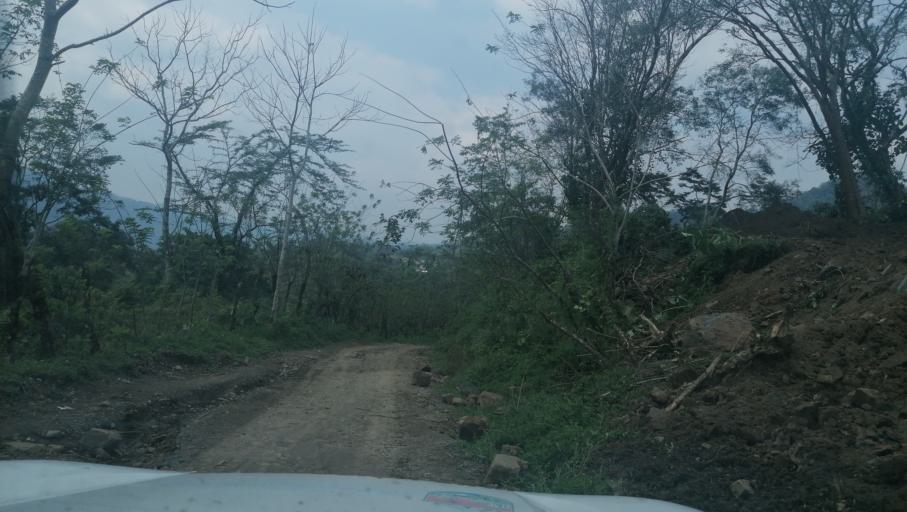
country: MX
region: Chiapas
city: Ostuacan
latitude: 17.3593
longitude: -93.3240
